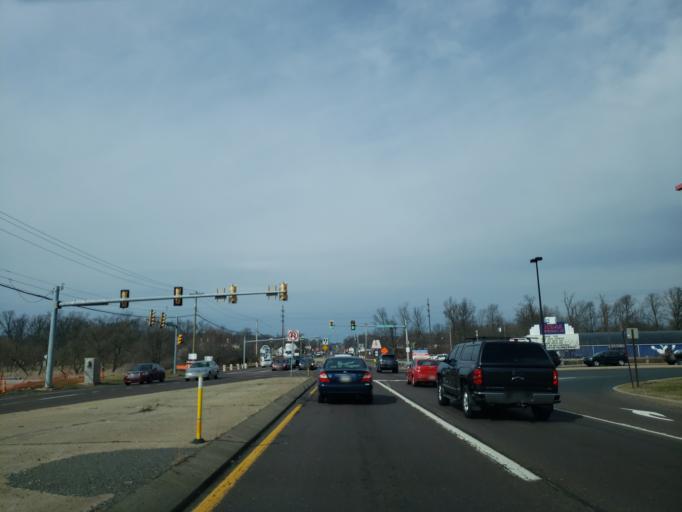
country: US
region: Pennsylvania
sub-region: Bucks County
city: Quakertown
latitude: 40.4486
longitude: -75.3613
